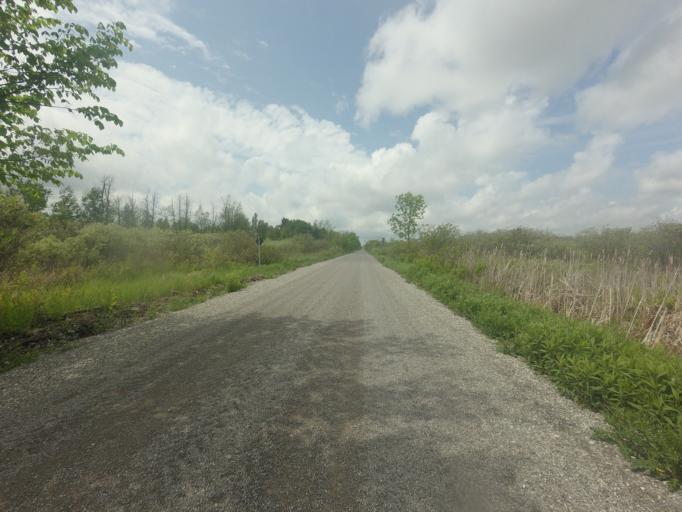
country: CA
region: Ontario
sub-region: Lanark County
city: Smiths Falls
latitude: 44.9396
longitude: -76.0387
